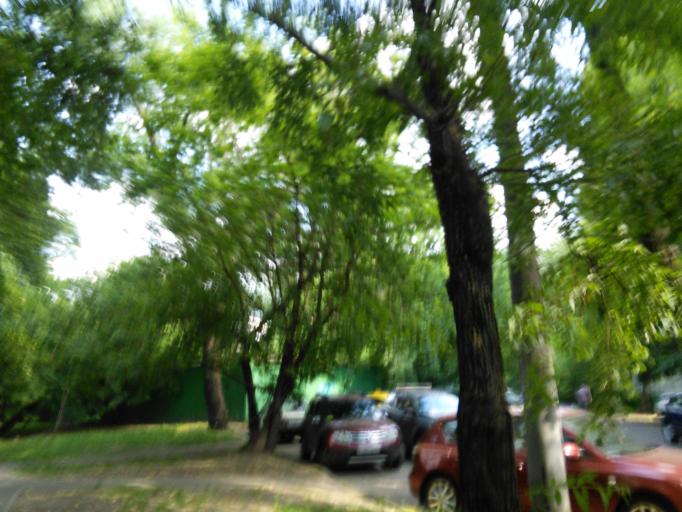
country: RU
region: Moskovskaya
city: Bogorodskoye
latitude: 55.7945
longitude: 37.7209
